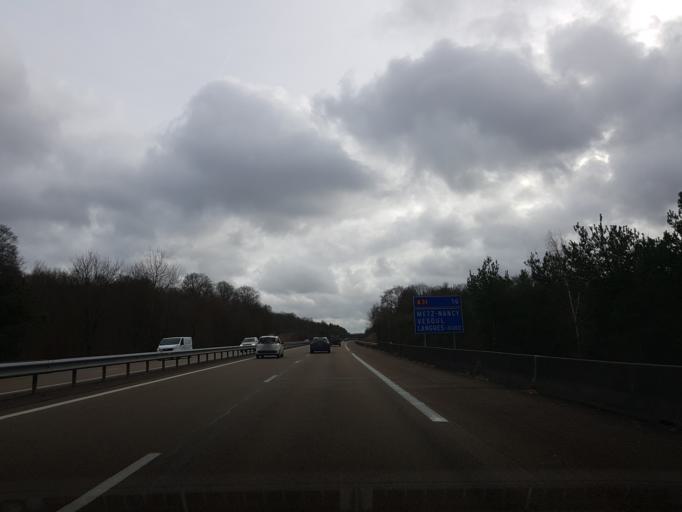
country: FR
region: Champagne-Ardenne
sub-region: Departement de la Haute-Marne
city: Chamarandes-Choignes
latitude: 48.0242
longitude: 5.0916
